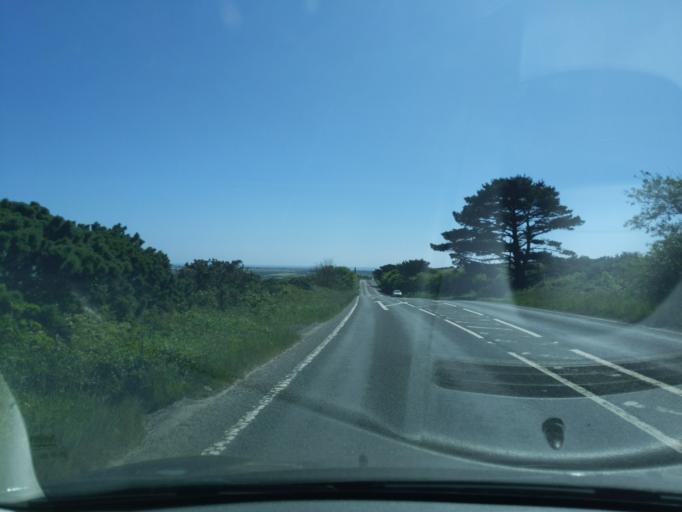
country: GB
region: England
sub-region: Cornwall
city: Wendron
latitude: 50.1343
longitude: -5.2232
